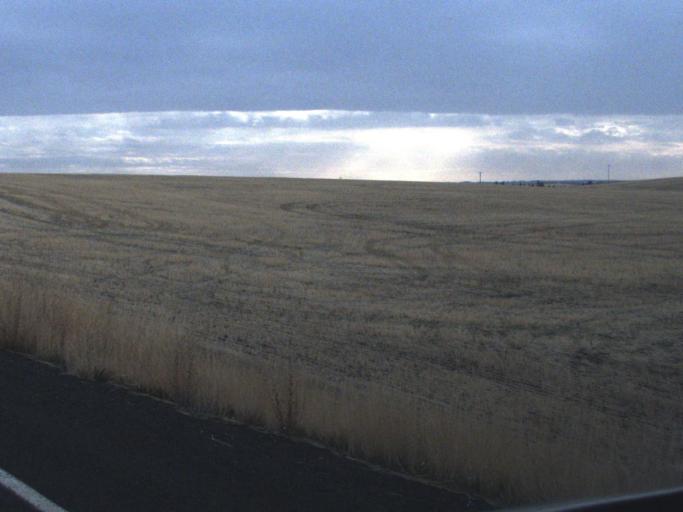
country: US
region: Washington
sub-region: Lincoln County
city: Davenport
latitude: 47.8420
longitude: -118.2129
